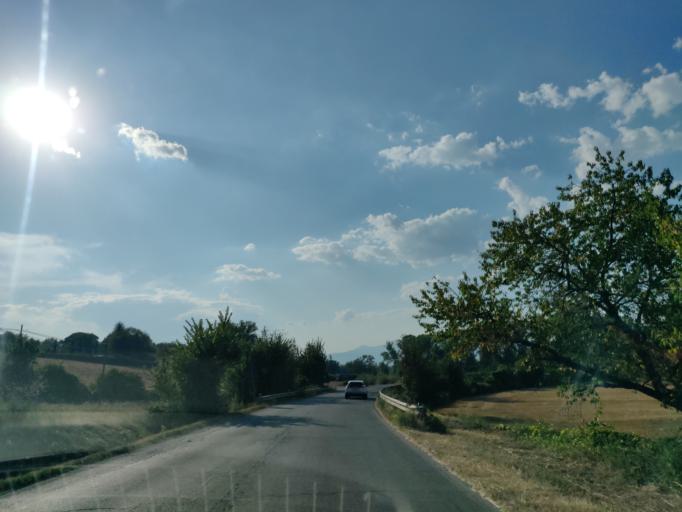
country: IT
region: Latium
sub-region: Provincia di Viterbo
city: Acquapendente
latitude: 42.7619
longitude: 11.8578
